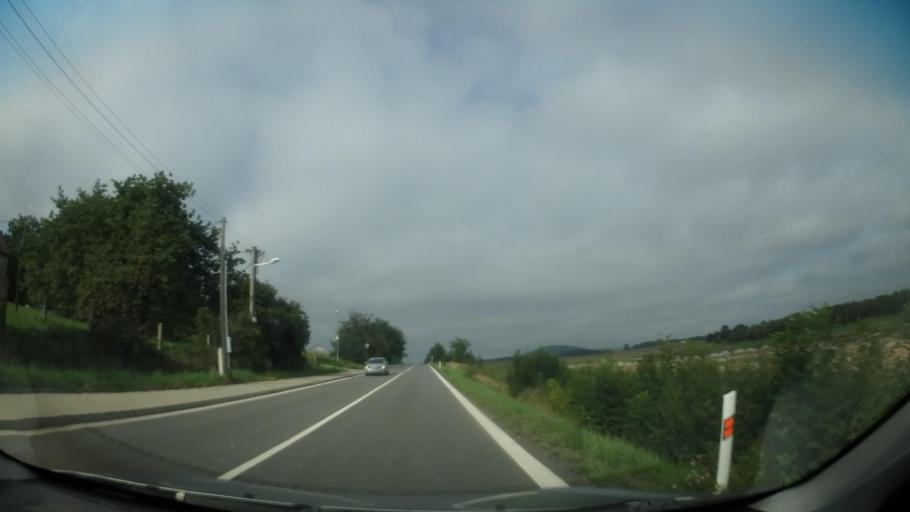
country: CZ
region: Central Bohemia
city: Bystrice
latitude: 49.7594
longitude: 14.6555
